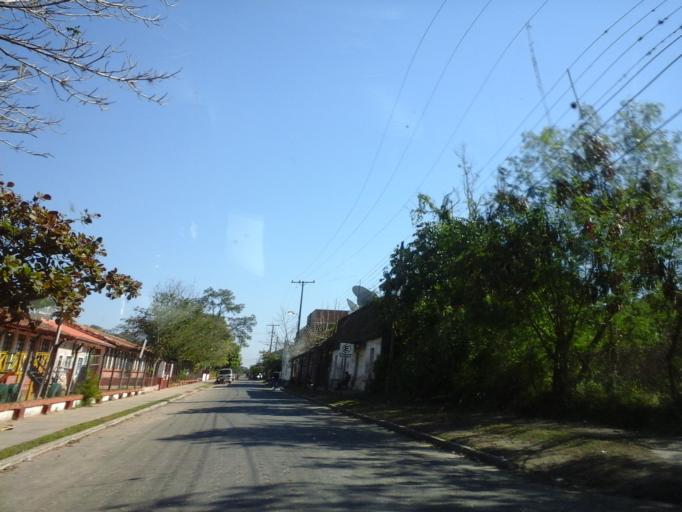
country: PY
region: Neembucu
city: Pilar
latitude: -26.8605
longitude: -58.3036
